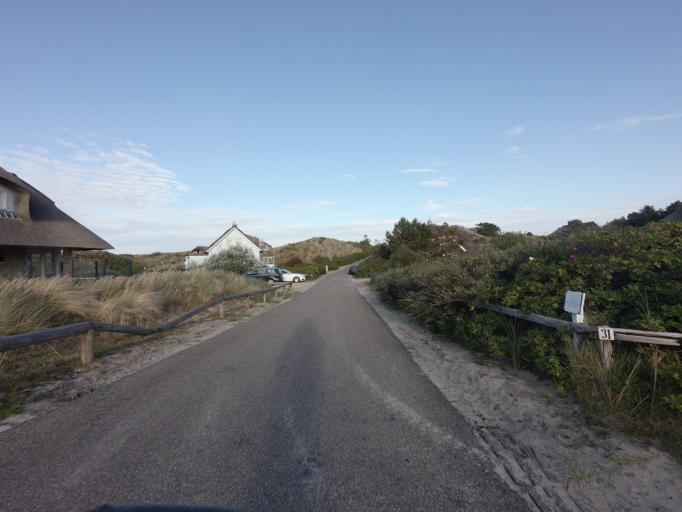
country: NL
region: Friesland
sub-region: Gemeente Ameland
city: Nes
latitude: 53.4580
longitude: 5.7981
